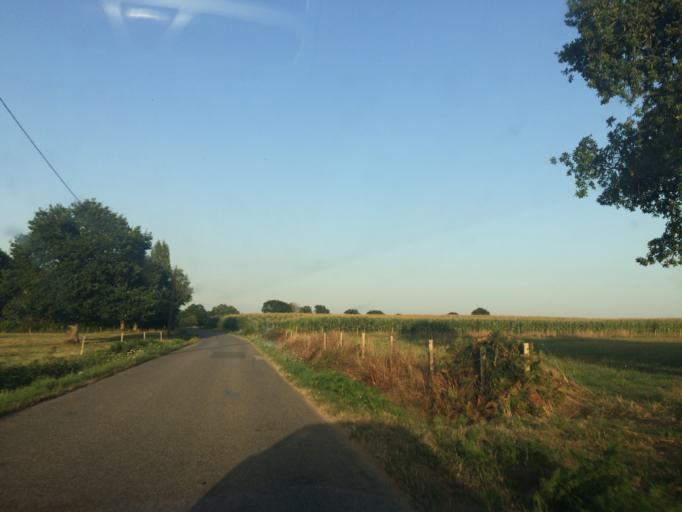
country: FR
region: Brittany
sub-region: Departement du Morbihan
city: Beganne
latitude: 47.6364
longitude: -2.2238
